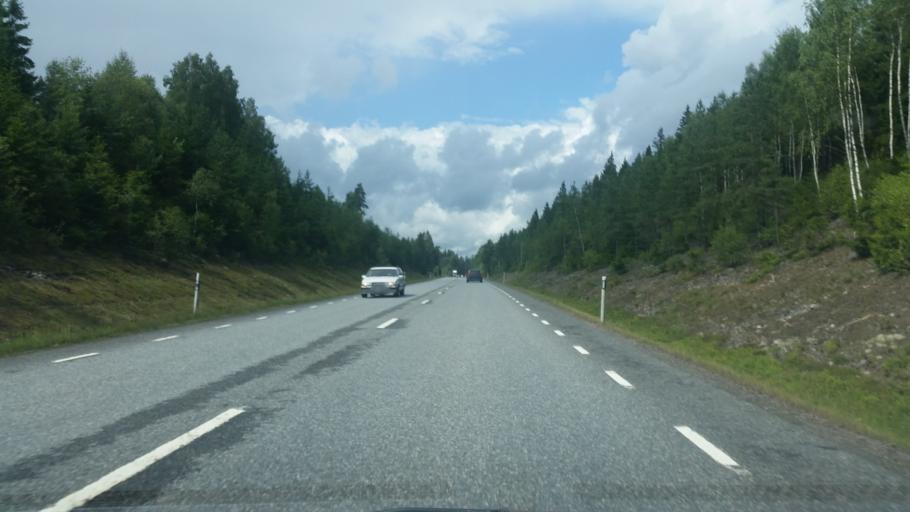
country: SE
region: Vaestra Goetaland
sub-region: Tranemo Kommun
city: Langhem
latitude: 57.5899
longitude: 13.2031
